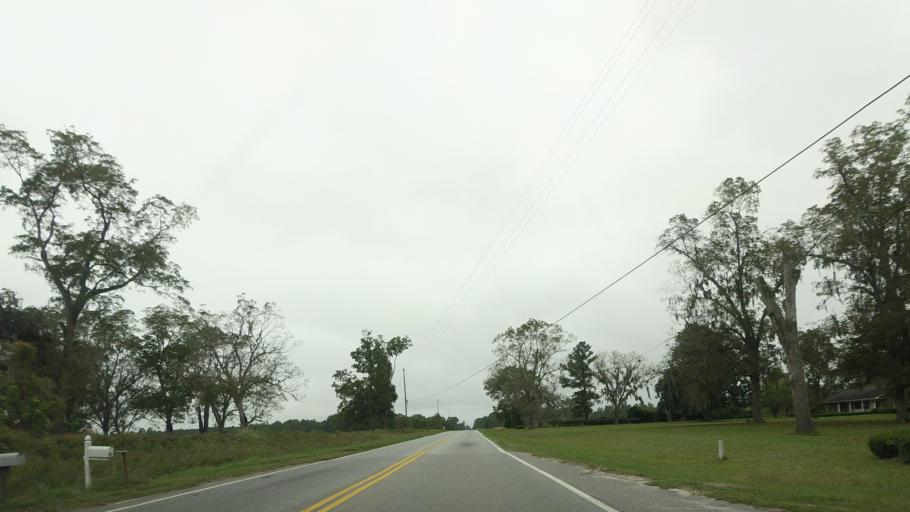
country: US
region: Georgia
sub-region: Lowndes County
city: Valdosta
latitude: 30.8121
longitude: -83.2353
